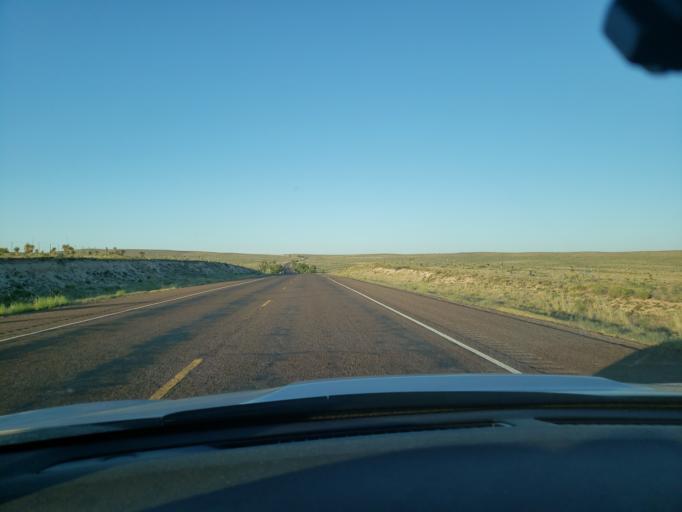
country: US
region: Texas
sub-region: El Paso County
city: Homestead Meadows South
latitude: 31.8295
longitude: -105.8701
